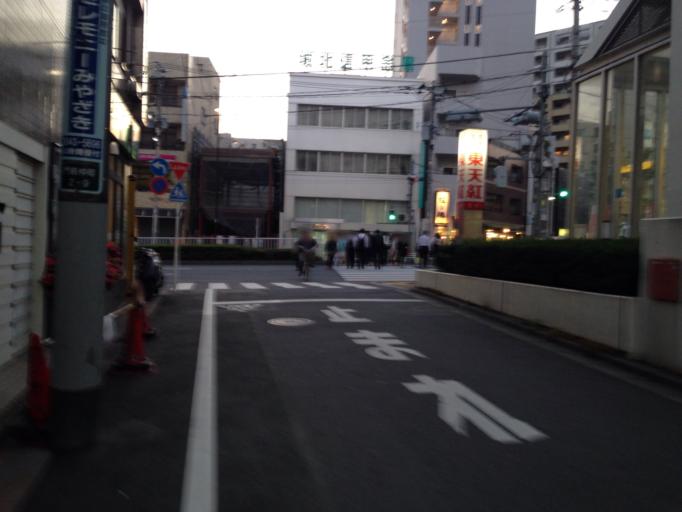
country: JP
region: Tokyo
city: Urayasu
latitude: 35.6733
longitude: 139.7959
